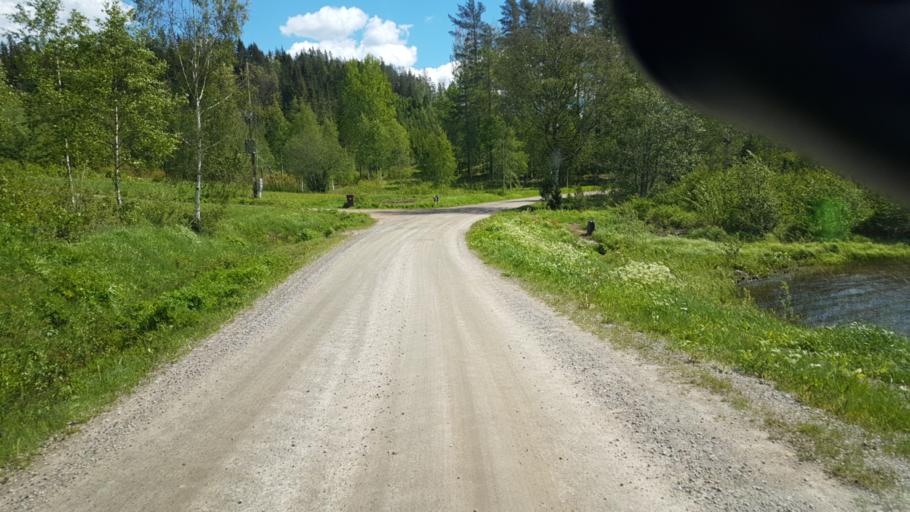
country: SE
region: Vaermland
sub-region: Arvika Kommun
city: Arvika
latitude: 59.7124
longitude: 12.8499
